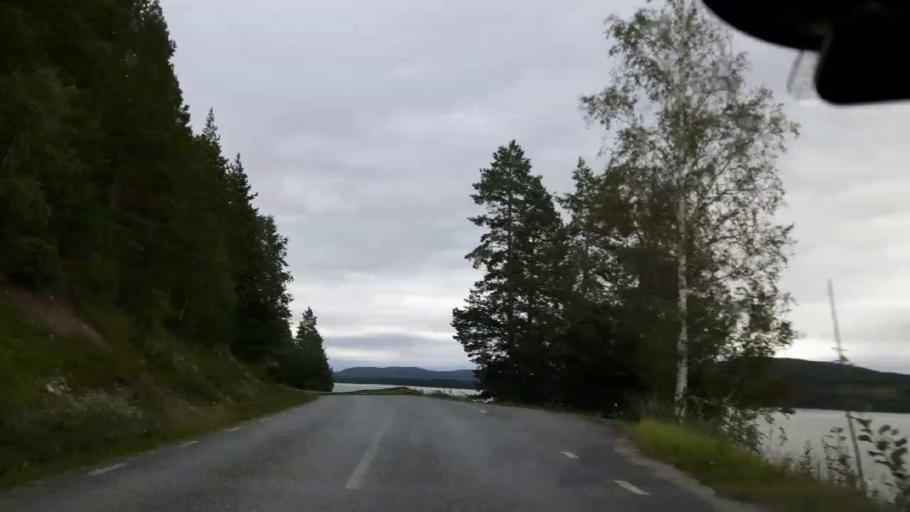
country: SE
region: Jaemtland
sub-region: Braecke Kommun
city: Braecke
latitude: 62.8650
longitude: 15.6185
